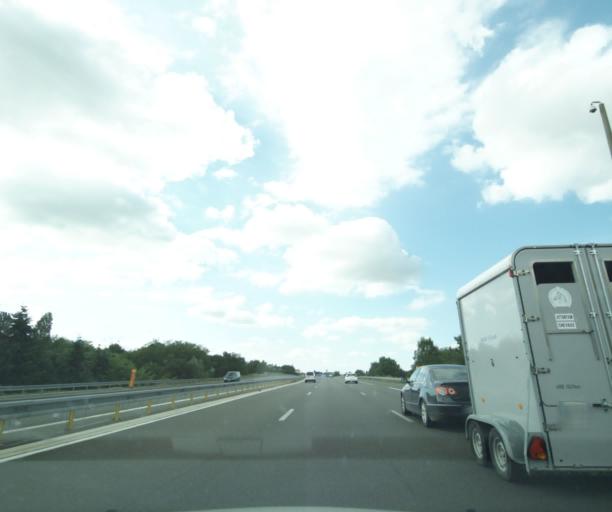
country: FR
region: Centre
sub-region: Departement du Loiret
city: Saint-Pryve-Saint-Mesmin
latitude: 47.8890
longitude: 1.8588
